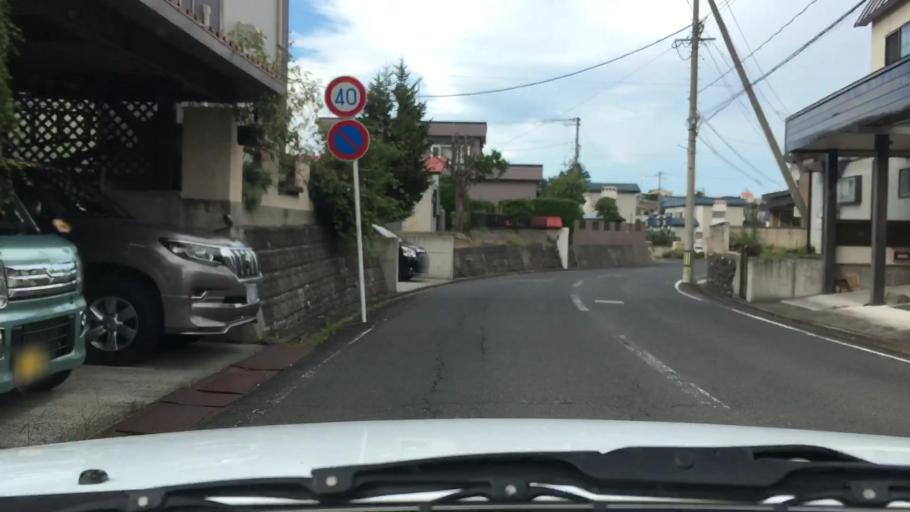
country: JP
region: Aomori
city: Hirosaki
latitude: 40.5755
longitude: 140.4539
